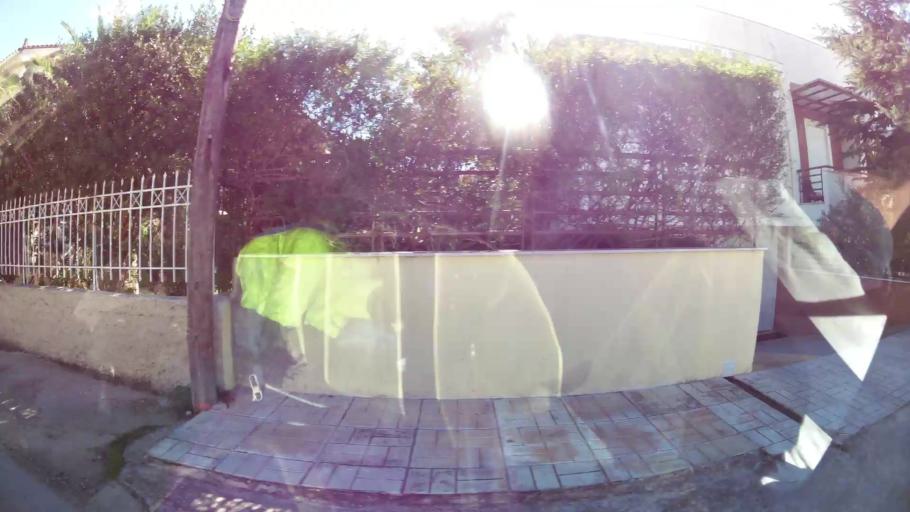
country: GR
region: Attica
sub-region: Nomarchia Anatolikis Attikis
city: Vari
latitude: 37.8382
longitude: 23.8127
